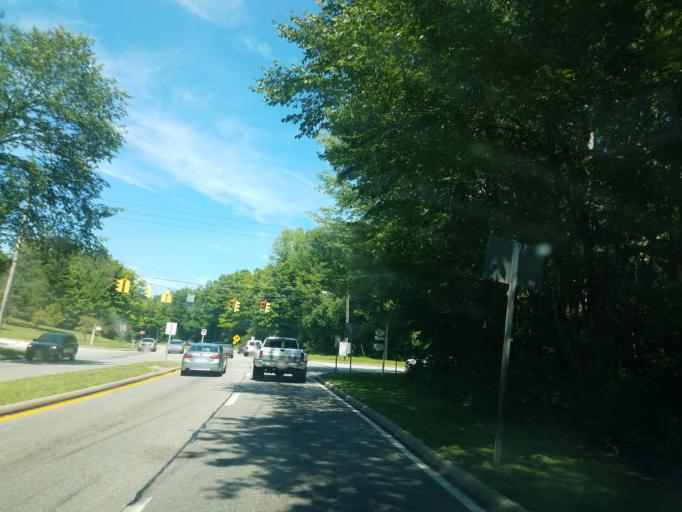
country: US
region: Ohio
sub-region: Cuyahoga County
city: Gates Mills
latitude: 41.5207
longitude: -81.4251
